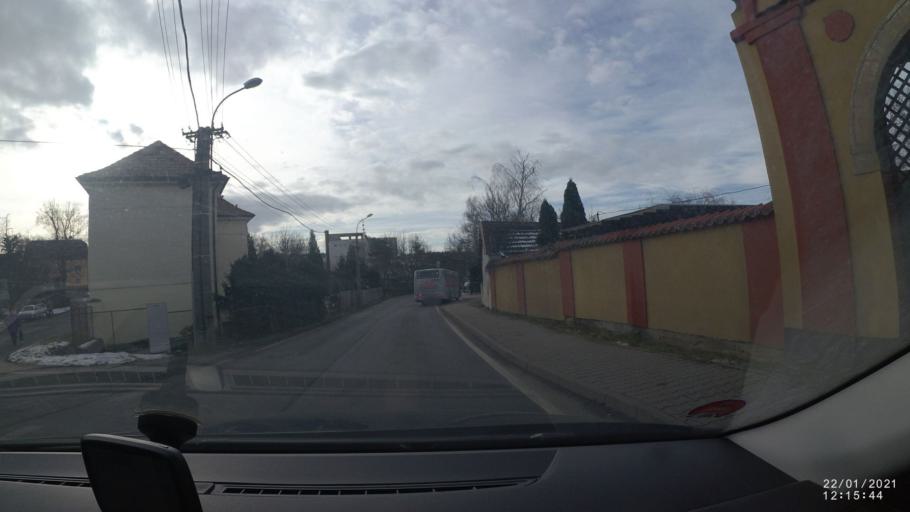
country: CZ
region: Plzensky
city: Dysina
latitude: 49.7573
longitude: 13.4579
